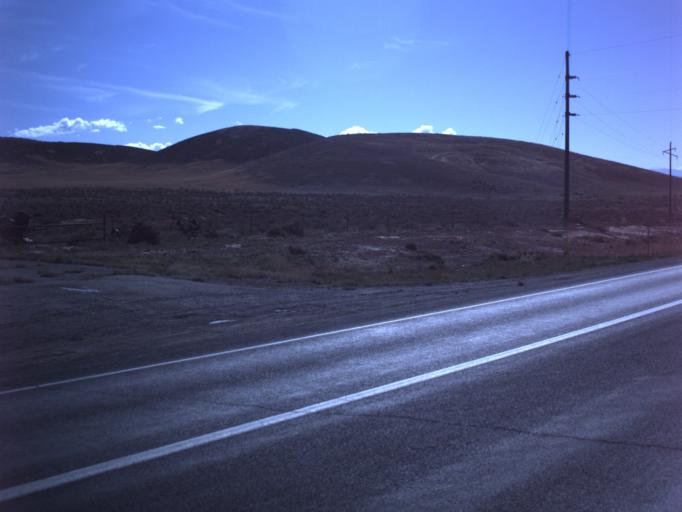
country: US
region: Utah
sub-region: Sanpete County
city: Gunnison
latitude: 39.2094
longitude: -111.8486
